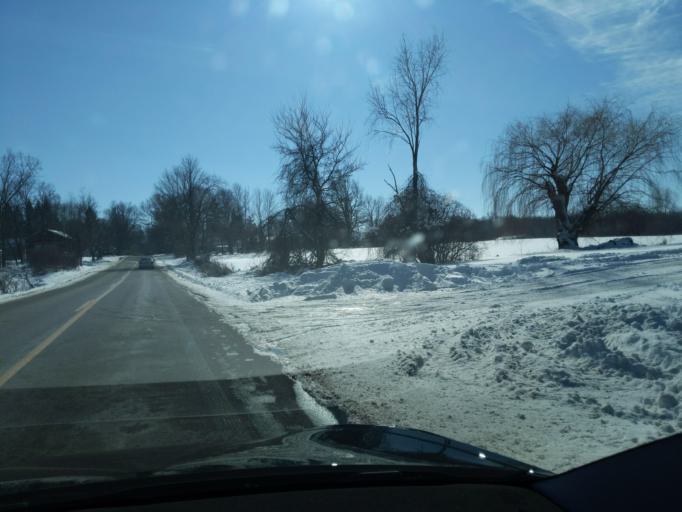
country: US
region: Michigan
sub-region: Livingston County
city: Fowlerville
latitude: 42.5277
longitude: -84.0681
